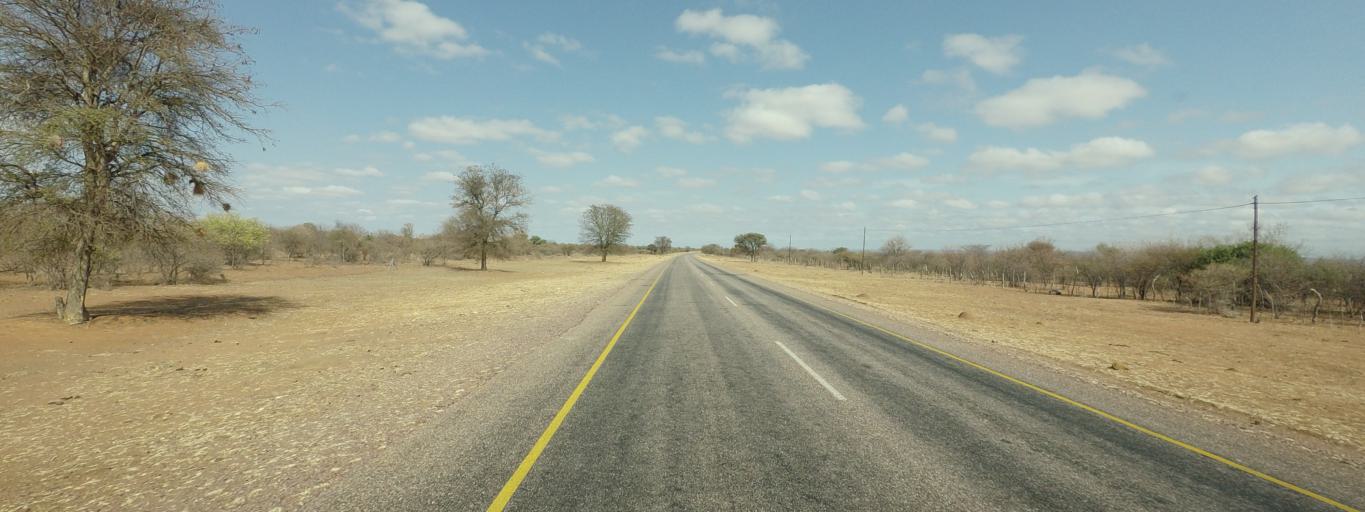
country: BW
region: Central
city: Ratholo
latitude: -22.8133
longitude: 27.5466
